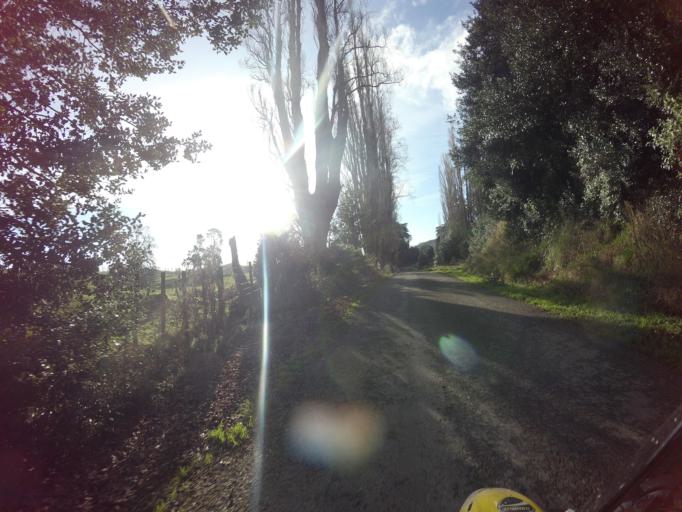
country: NZ
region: Hawke's Bay
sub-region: Wairoa District
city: Wairoa
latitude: -38.7726
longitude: 177.5657
